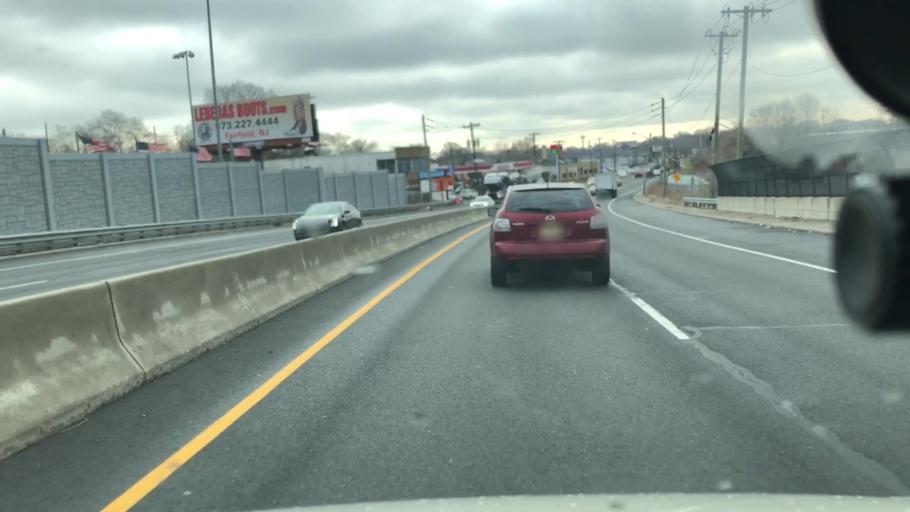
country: US
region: New Jersey
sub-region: Union County
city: Hillside
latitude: 40.6989
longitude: -74.2286
